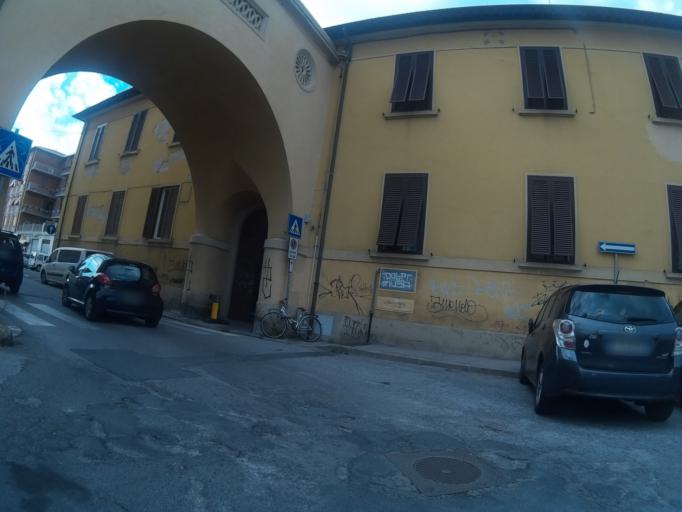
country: IT
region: Tuscany
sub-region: Provincia di Livorno
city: Livorno
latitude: 43.5582
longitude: 10.3180
